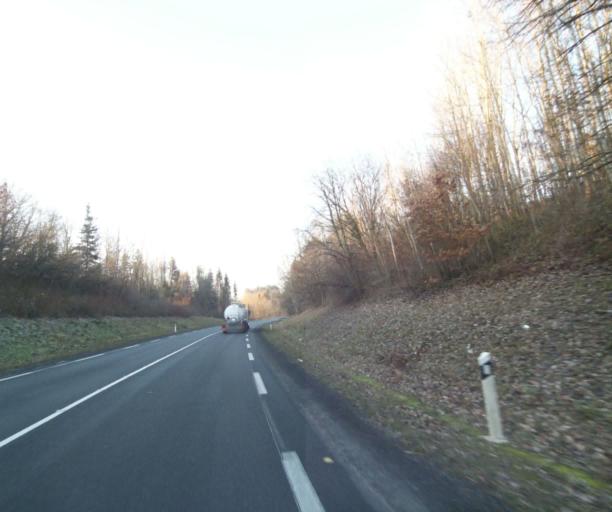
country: FR
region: Champagne-Ardenne
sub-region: Departement de la Haute-Marne
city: Bienville
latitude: 48.5652
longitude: 5.0365
